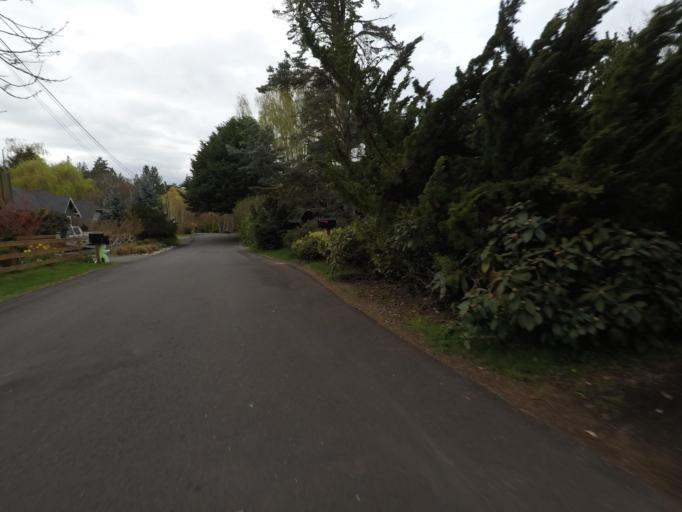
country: US
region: Washington
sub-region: Snohomish County
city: Edmonds
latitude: 47.8224
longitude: -122.3649
